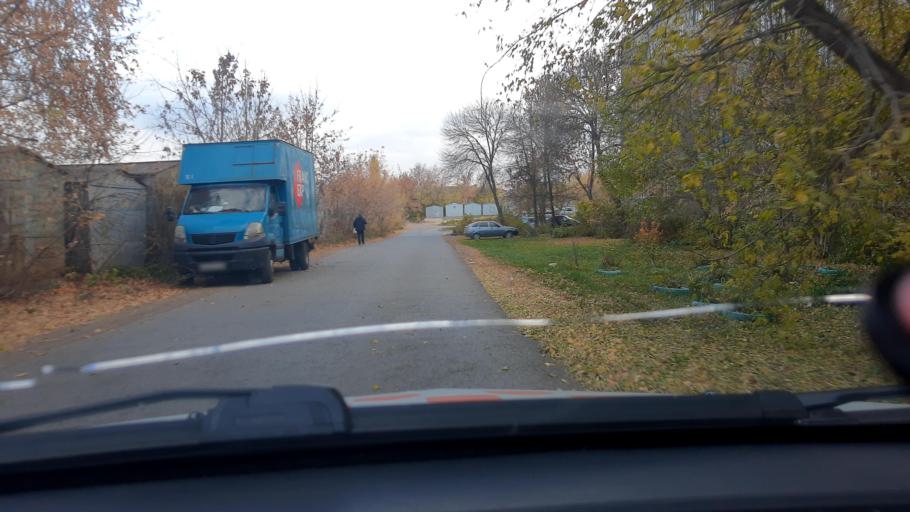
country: RU
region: Bashkortostan
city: Ufa
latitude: 54.8101
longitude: 56.1375
